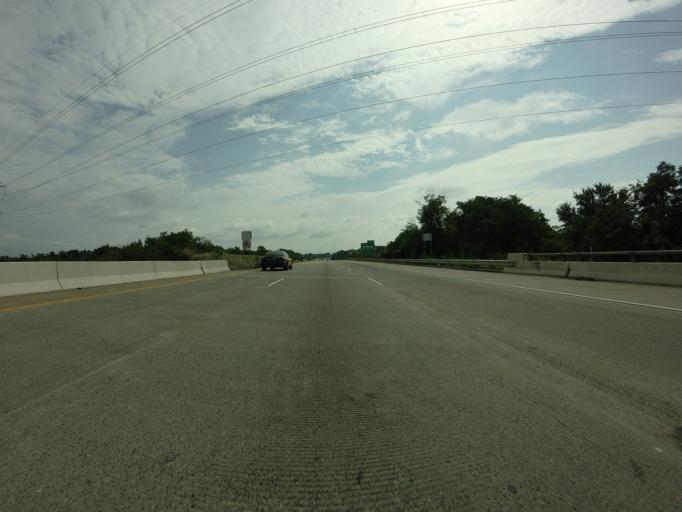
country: US
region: Delaware
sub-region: New Castle County
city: Wilmington Manor
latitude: 39.7148
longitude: -75.5780
